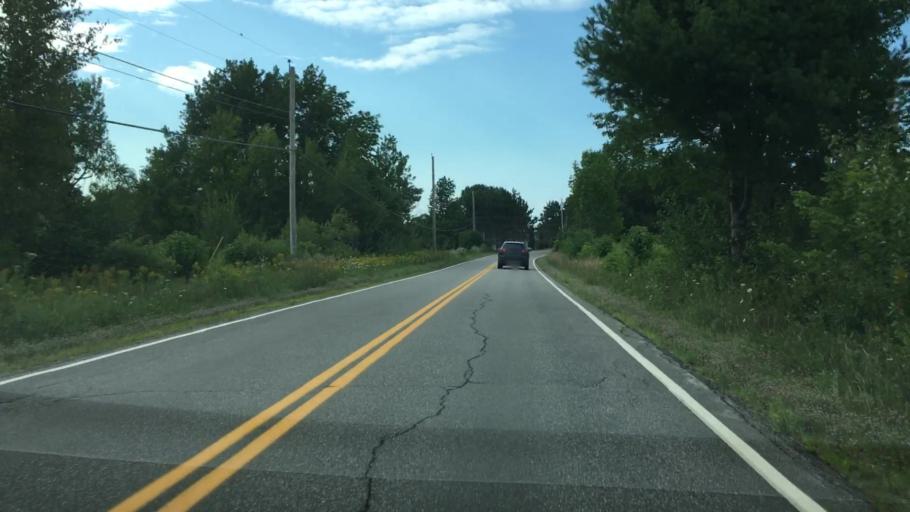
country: US
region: Maine
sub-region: Waldo County
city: Belfast
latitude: 44.3775
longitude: -69.0330
